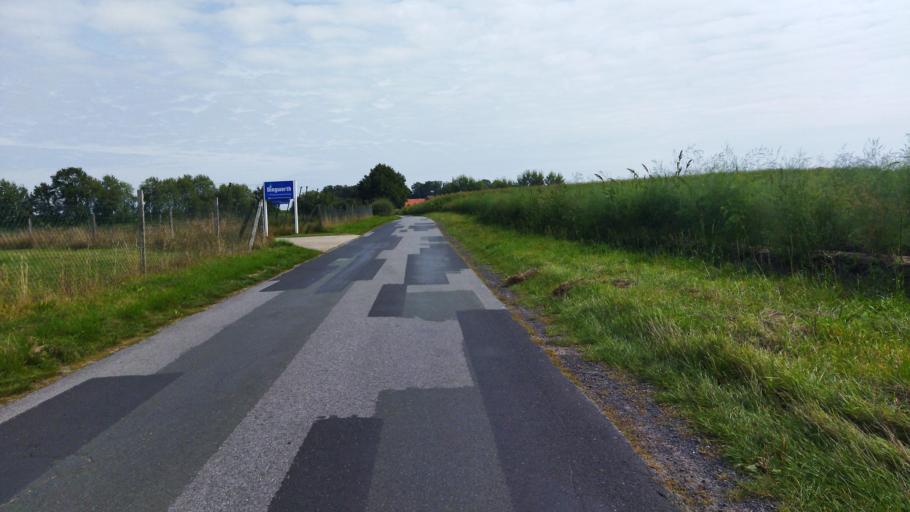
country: DE
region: Lower Saxony
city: Glandorf
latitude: 52.0787
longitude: 8.0259
